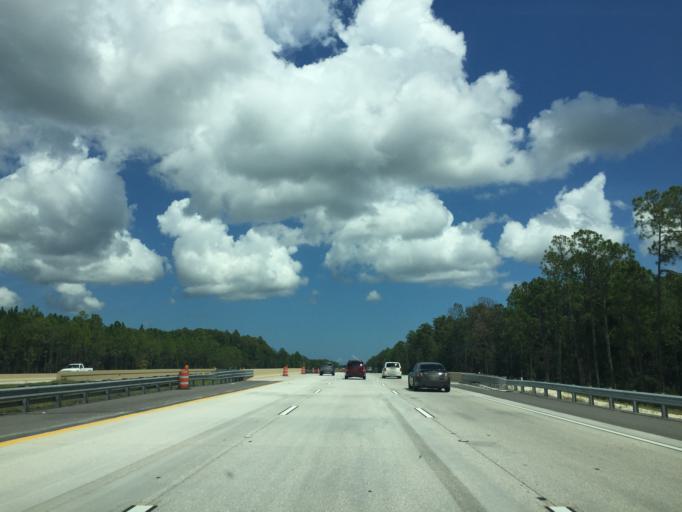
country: US
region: Florida
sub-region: Volusia County
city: Lake Helen
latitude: 29.0766
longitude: -81.1757
